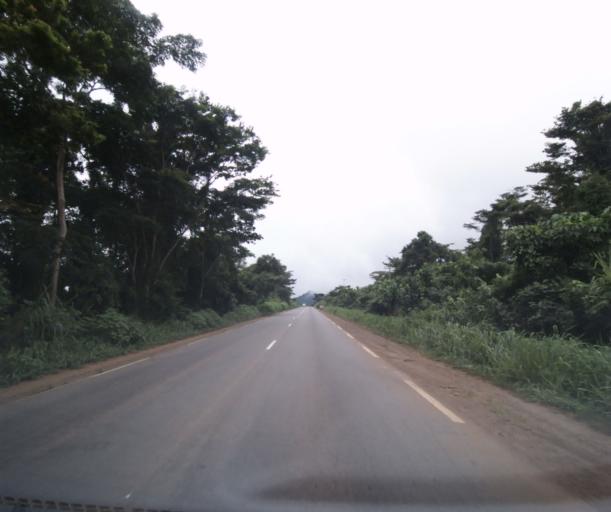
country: CM
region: Centre
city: Mbankomo
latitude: 3.7994
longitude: 11.3515
